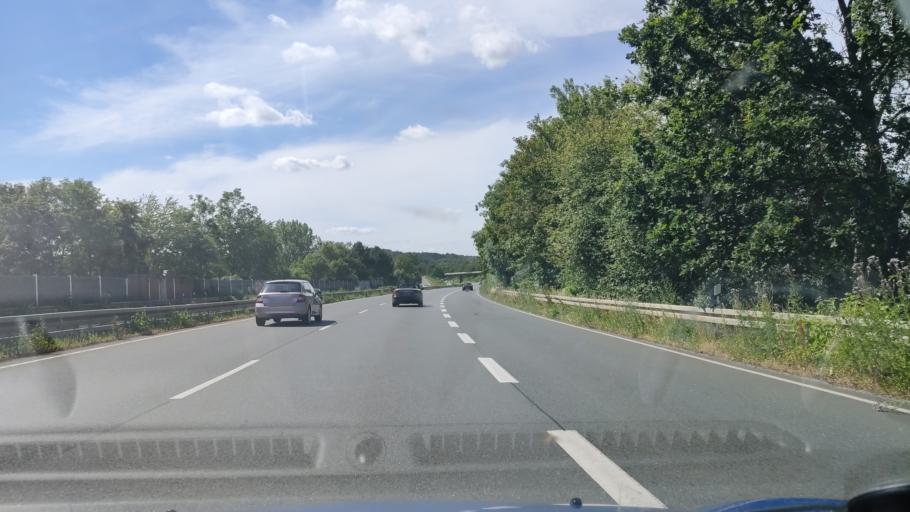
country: DE
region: Lower Saxony
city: Ronnenberg
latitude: 52.3481
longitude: 9.6617
